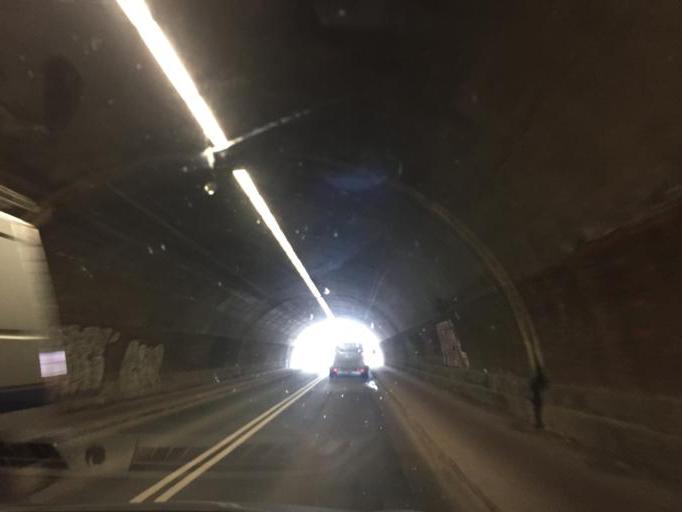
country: DK
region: South Denmark
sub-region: Odense Kommune
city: Odense
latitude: 55.4013
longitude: 10.3783
